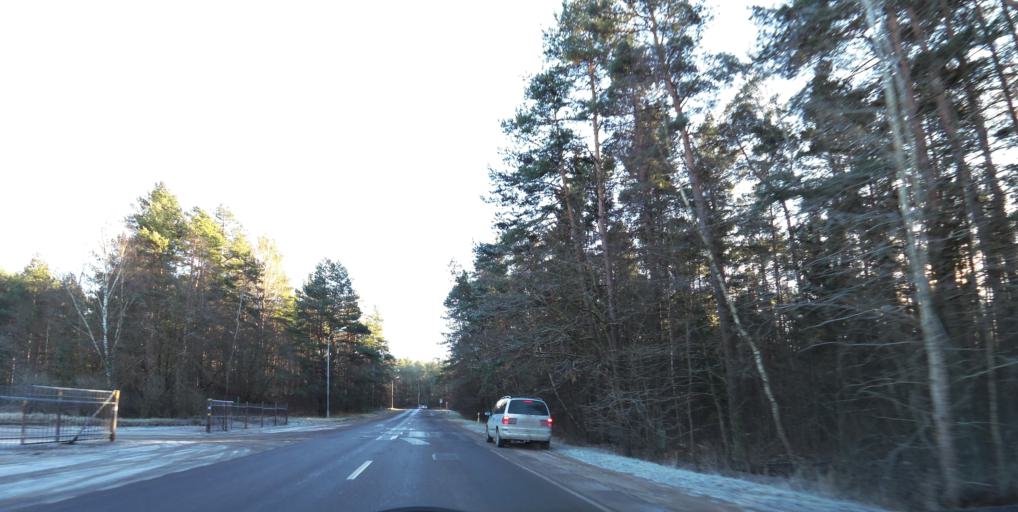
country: LT
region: Vilnius County
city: Lazdynai
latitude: 54.6408
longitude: 25.1767
